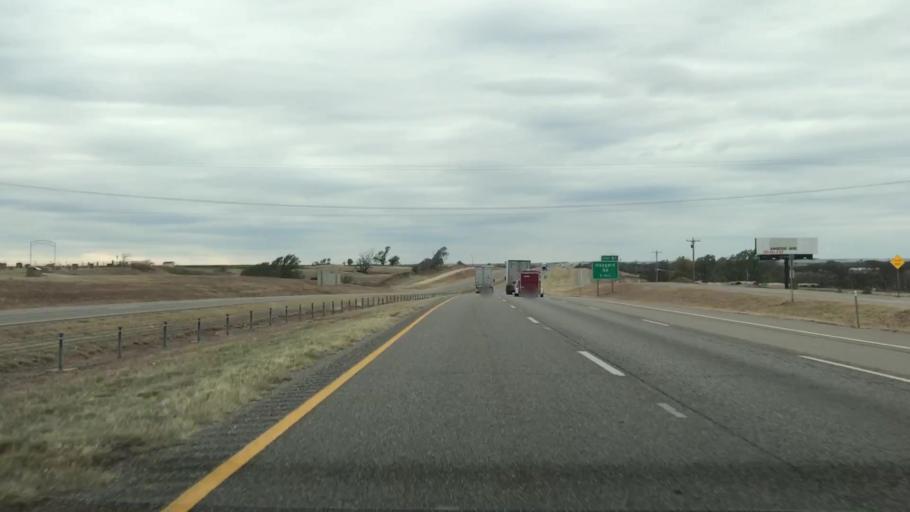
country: US
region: Oklahoma
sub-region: Custer County
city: Clinton
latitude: 35.4802
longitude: -99.0285
